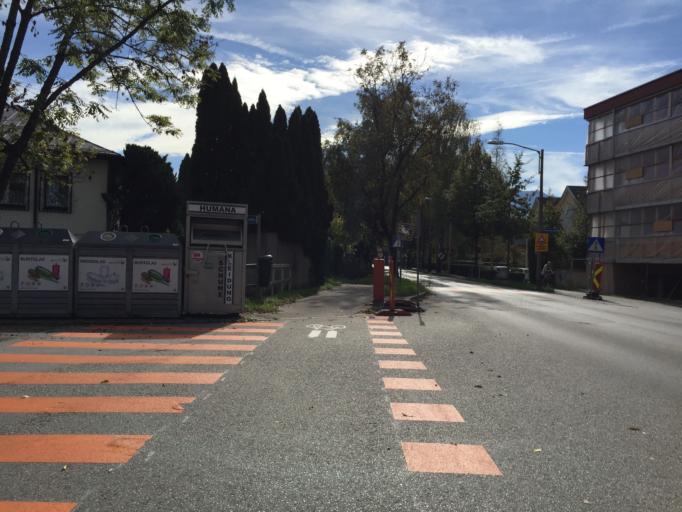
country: AT
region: Salzburg
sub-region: Salzburg Stadt
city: Salzburg
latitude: 47.7899
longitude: 13.0279
